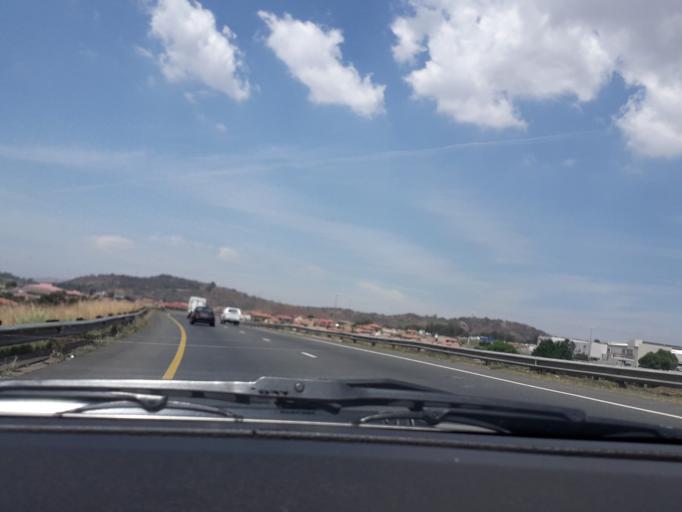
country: ZA
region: Gauteng
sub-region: City of Johannesburg Metropolitan Municipality
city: Johannesburg
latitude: -26.2611
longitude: 27.9867
